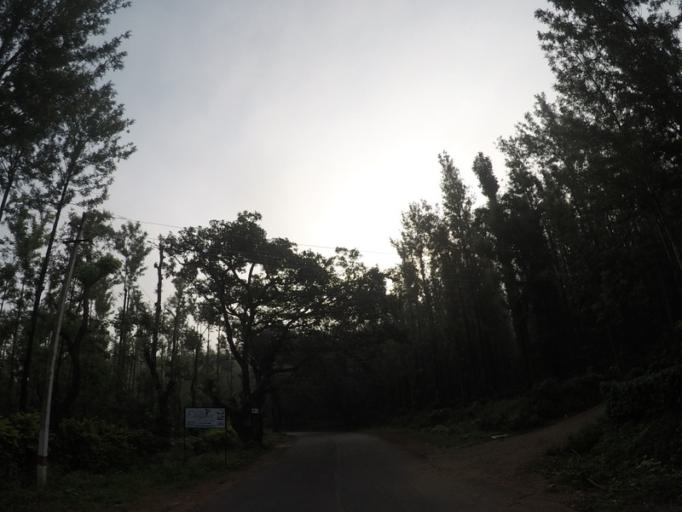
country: IN
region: Karnataka
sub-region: Chikmagalur
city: Chikmagalur
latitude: 13.3825
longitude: 75.7557
